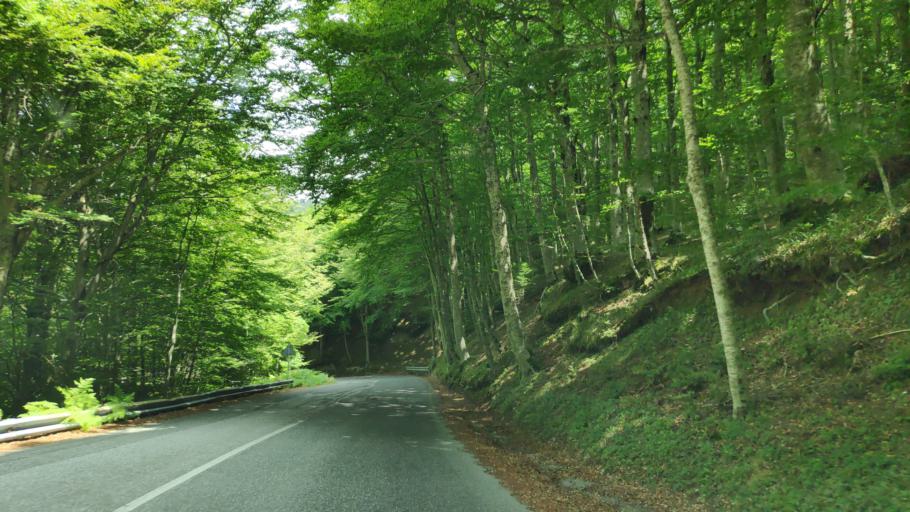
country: IT
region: Calabria
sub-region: Provincia di Vibo-Valentia
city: Mongiana
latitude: 38.5191
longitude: 16.3402
